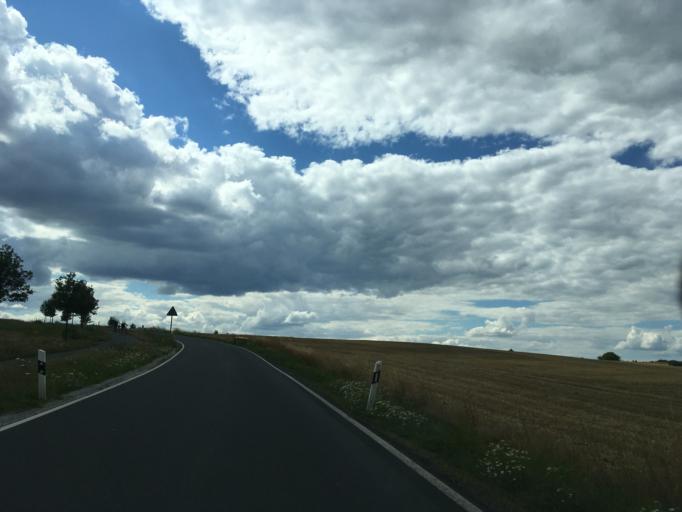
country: DE
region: Saxony
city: Wachau
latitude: 51.1572
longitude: 13.8971
